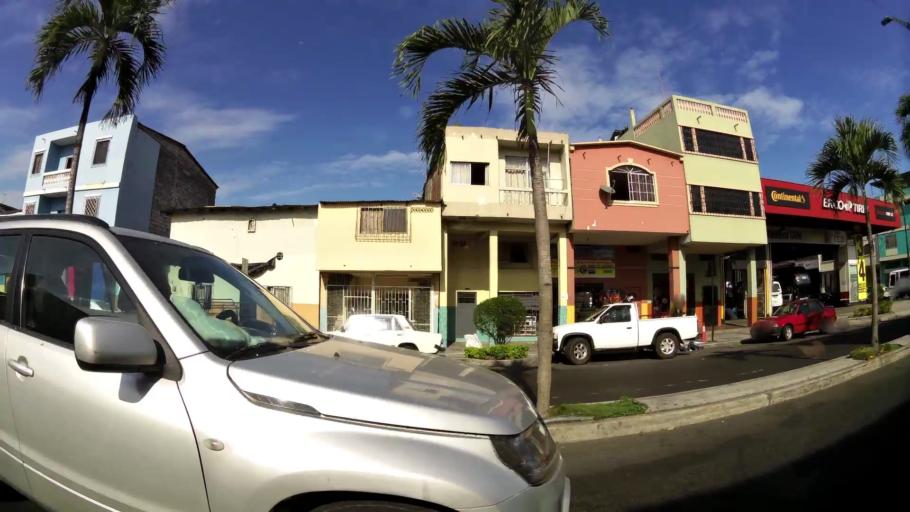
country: EC
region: Guayas
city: Guayaquil
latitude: -2.1966
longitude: -79.9144
